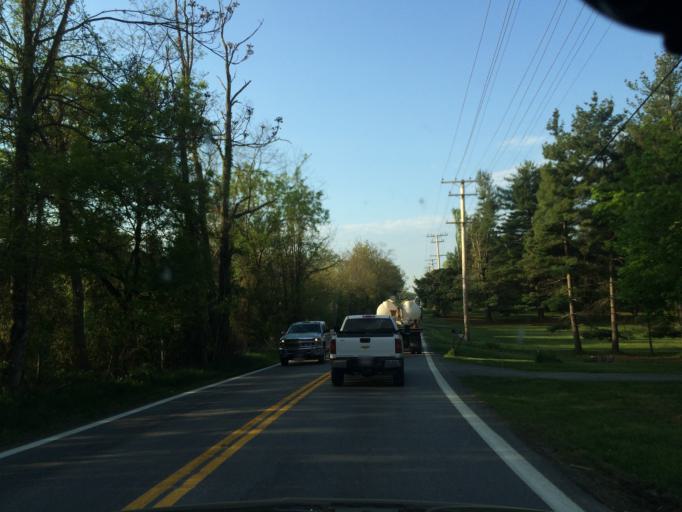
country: US
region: Maryland
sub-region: Carroll County
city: Sykesville
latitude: 39.3462
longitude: -77.0130
